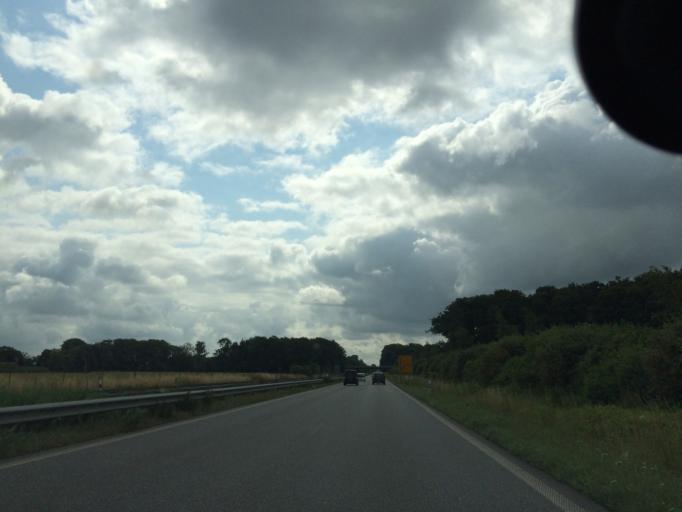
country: DE
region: Schleswig-Holstein
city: Tuttendorf
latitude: 54.3961
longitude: 10.0120
